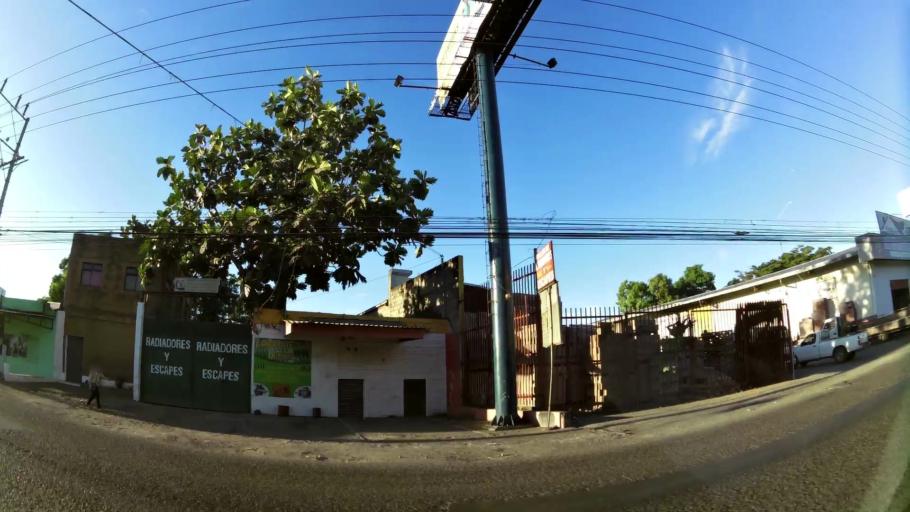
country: SV
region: San Miguel
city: San Miguel
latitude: 13.4632
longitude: -88.1669
